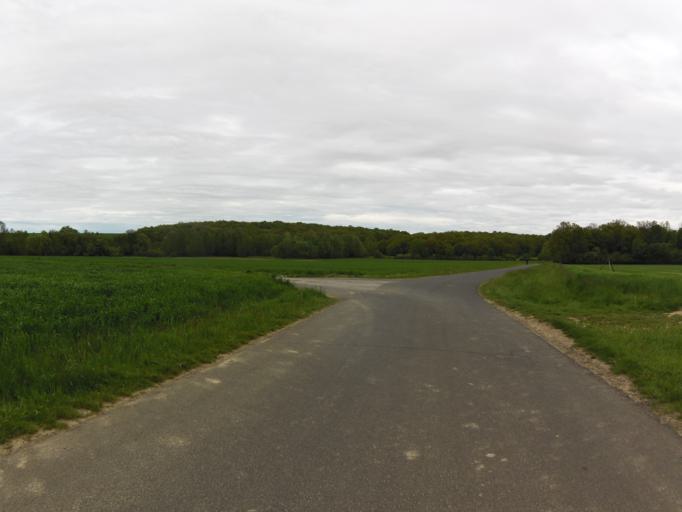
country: DE
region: Bavaria
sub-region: Regierungsbezirk Unterfranken
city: Kurnach
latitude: 49.8440
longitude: 10.0616
